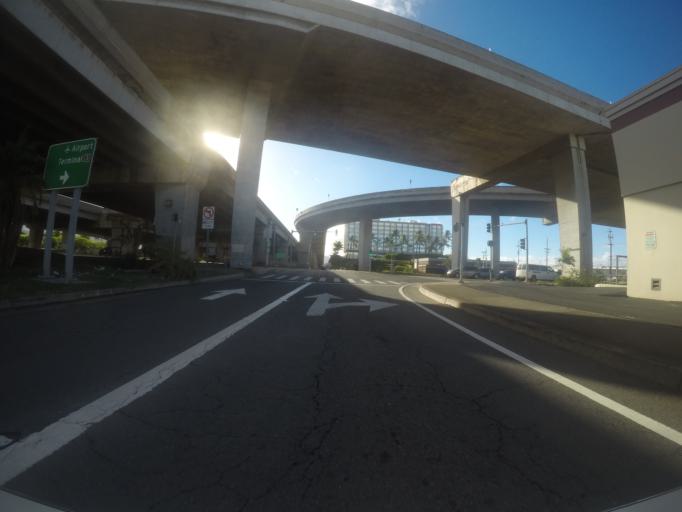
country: US
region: Hawaii
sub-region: Honolulu County
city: Halawa Heights
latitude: 21.3368
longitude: -157.9151
